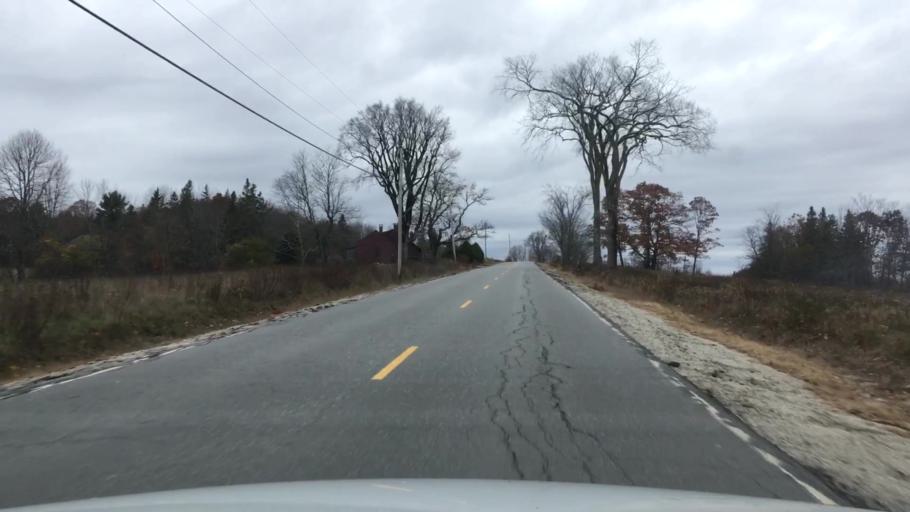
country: US
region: Maine
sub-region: Hancock County
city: Penobscot
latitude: 44.4384
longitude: -68.6339
